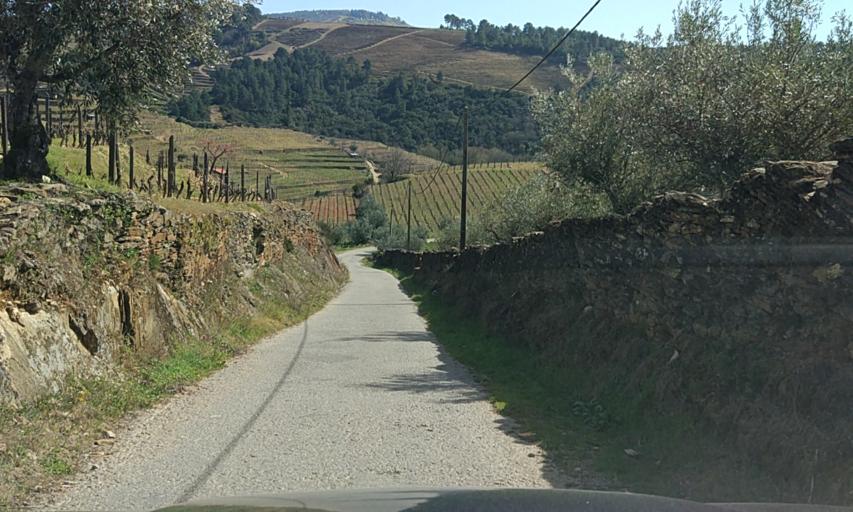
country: PT
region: Vila Real
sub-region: Sabrosa
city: Sabrosa
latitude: 41.3086
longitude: -7.5504
